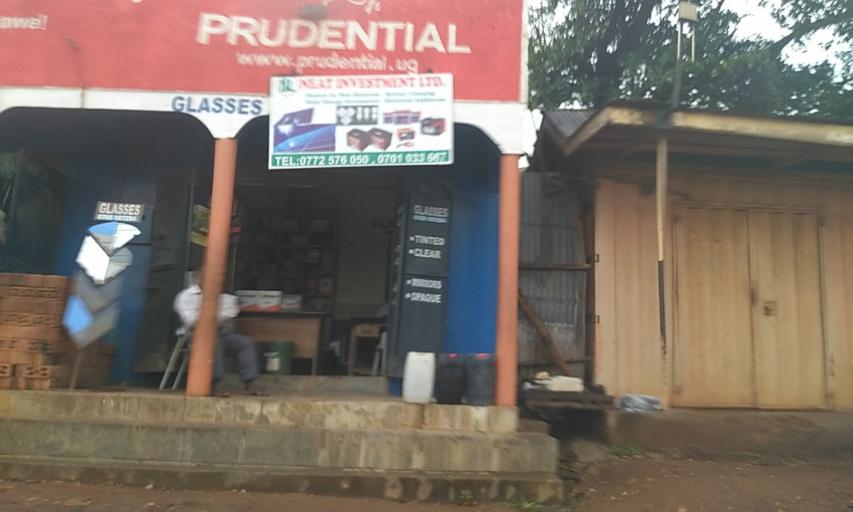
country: UG
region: Central Region
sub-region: Wakiso District
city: Bweyogerere
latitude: 0.3544
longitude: 32.6643
